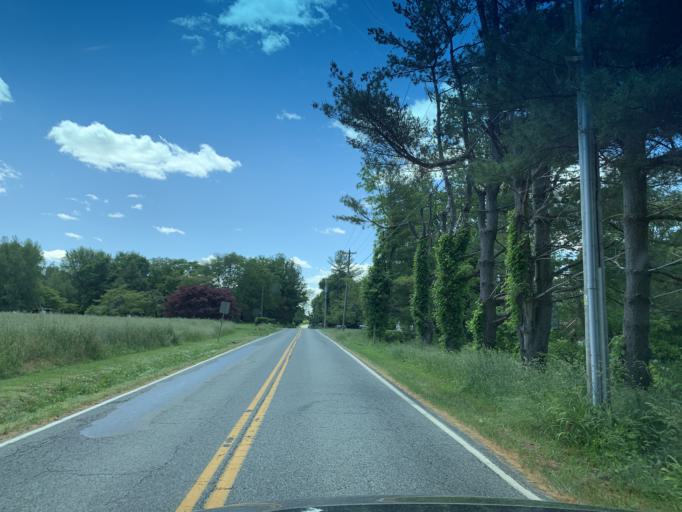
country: US
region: Maryland
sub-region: Cecil County
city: Rising Sun
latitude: 39.6964
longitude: -75.9887
